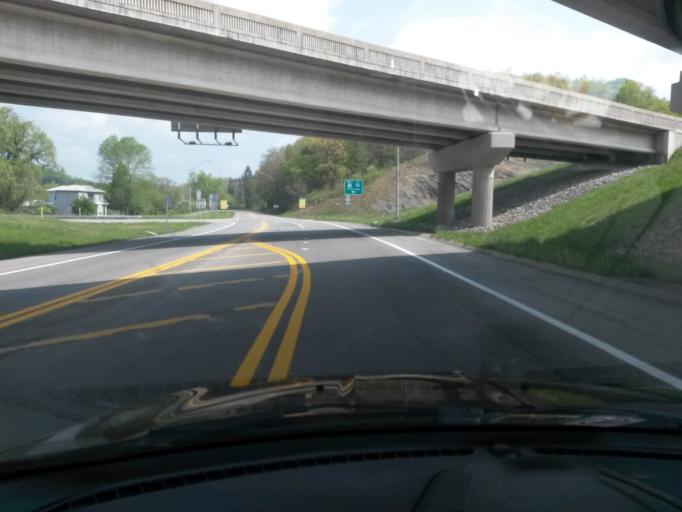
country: US
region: West Virginia
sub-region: Randolph County
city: Elkins
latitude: 38.9540
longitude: -79.8575
